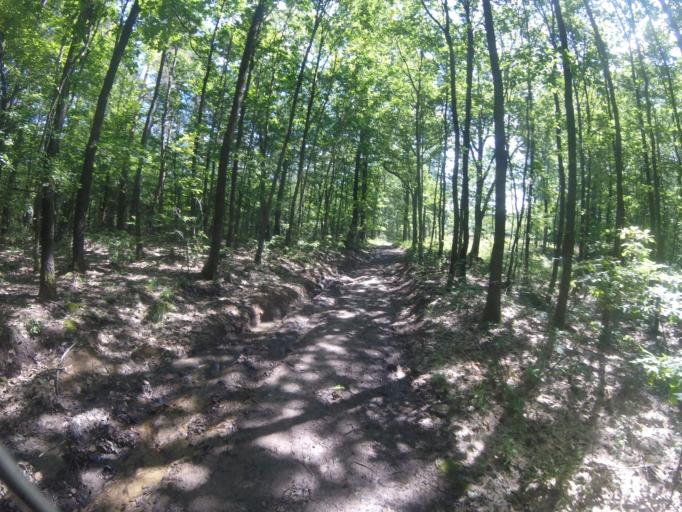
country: HU
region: Nograd
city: Matraverebely
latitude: 47.9297
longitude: 19.8011
